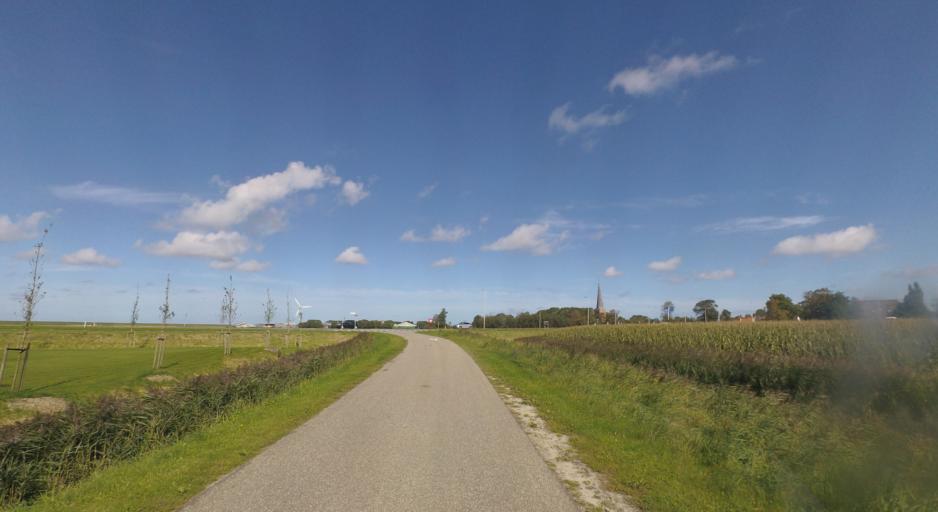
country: NL
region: Friesland
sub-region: Gemeente Dongeradeel
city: Holwerd
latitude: 53.3673
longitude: 5.8940
